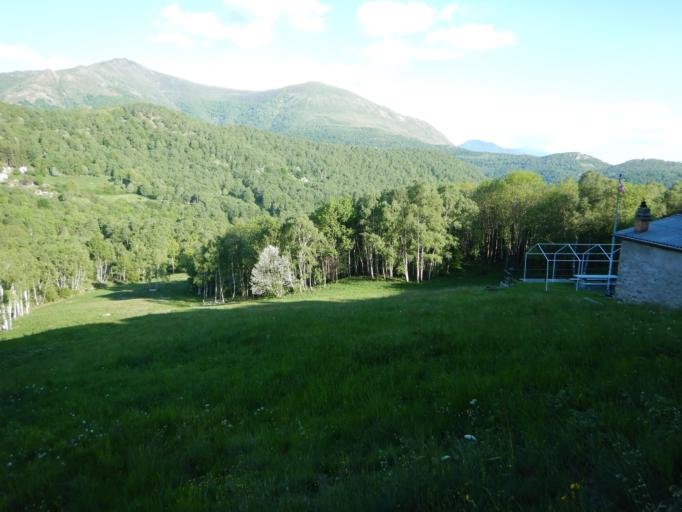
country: CH
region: Ticino
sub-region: Bellinzona District
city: Cadenazzo
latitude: 46.1320
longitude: 8.9632
